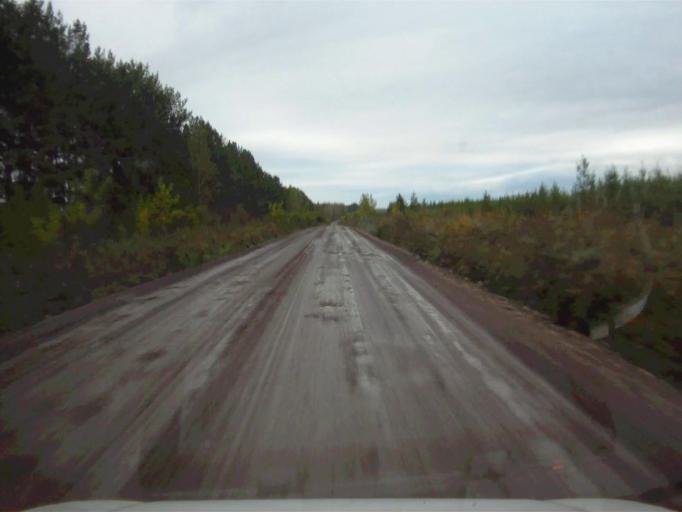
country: RU
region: Sverdlovsk
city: Mikhaylovsk
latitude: 56.1457
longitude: 59.2815
